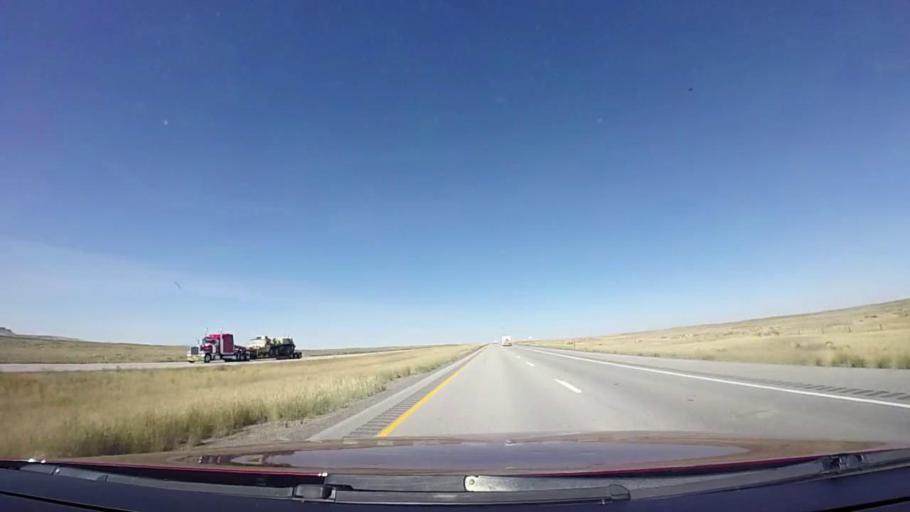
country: US
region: Wyoming
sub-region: Sweetwater County
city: Rock Springs
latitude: 41.6311
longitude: -108.3288
